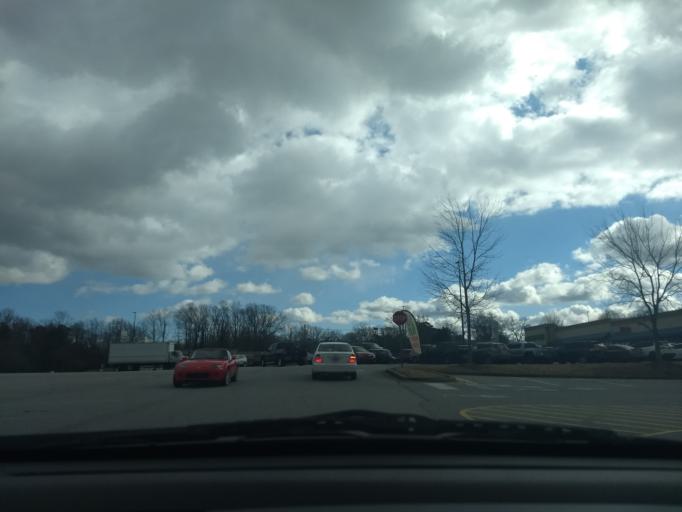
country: US
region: South Carolina
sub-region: Greenville County
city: Wade Hampton
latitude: 34.9075
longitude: -82.3315
